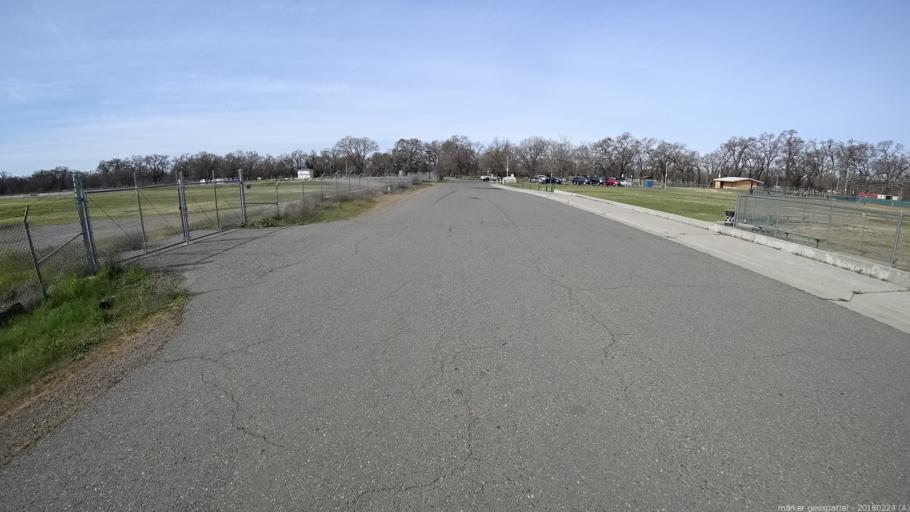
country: US
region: California
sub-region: Sacramento County
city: Rio Linda
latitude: 38.6801
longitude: -121.4446
